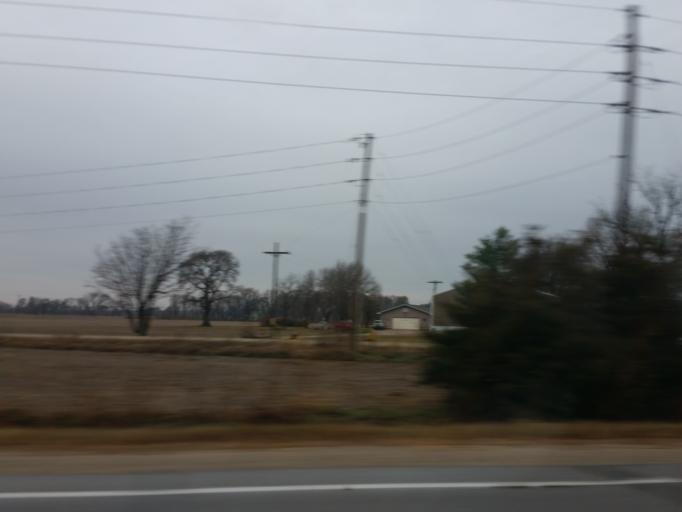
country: US
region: Iowa
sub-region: Black Hawk County
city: Elk Run Heights
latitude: 42.4018
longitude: -92.2587
